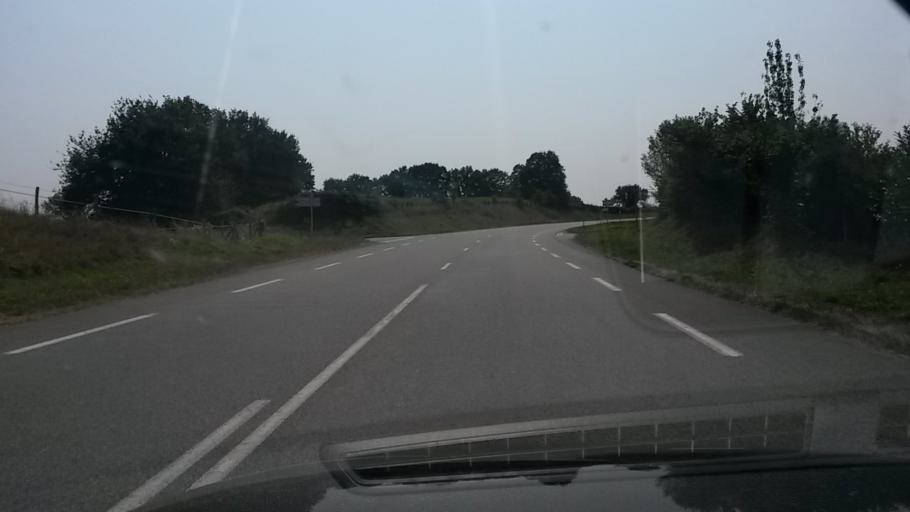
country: FR
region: Pays de la Loire
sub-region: Departement de la Mayenne
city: Chemaze
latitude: 47.7851
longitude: -0.7653
